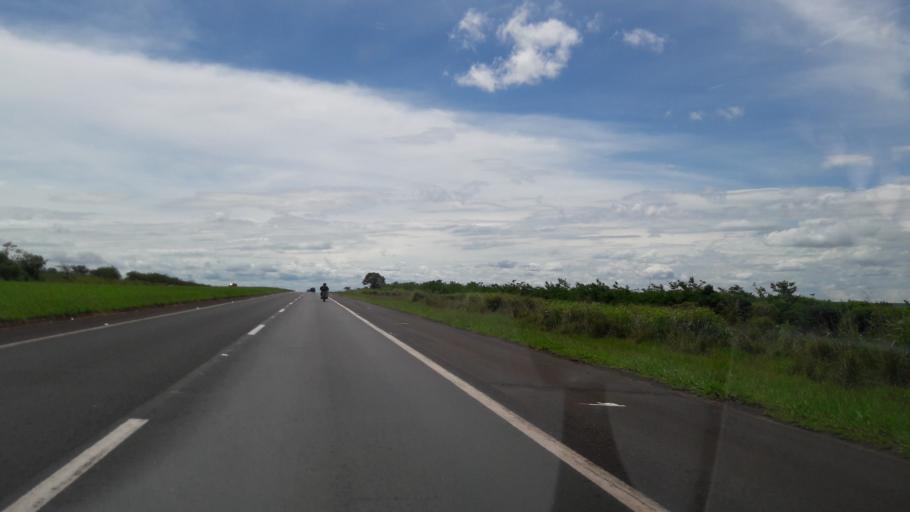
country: BR
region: Sao Paulo
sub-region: Avare
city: Avare
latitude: -22.9462
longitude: -48.8926
